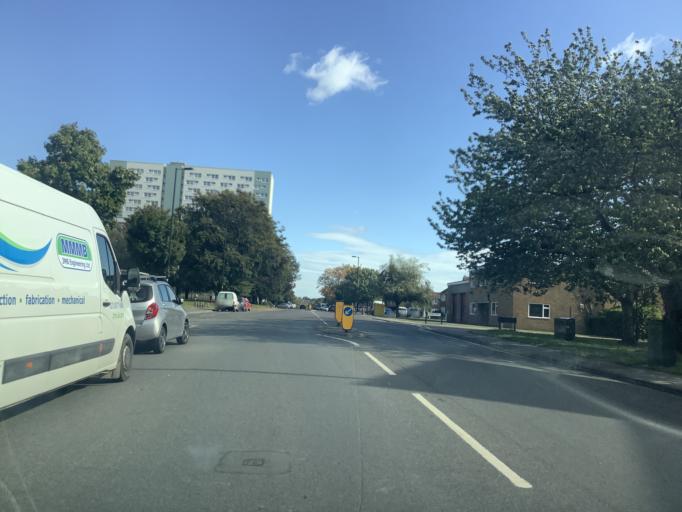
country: GB
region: England
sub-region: Hampshire
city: Marchwood
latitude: 50.9268
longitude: -1.4490
